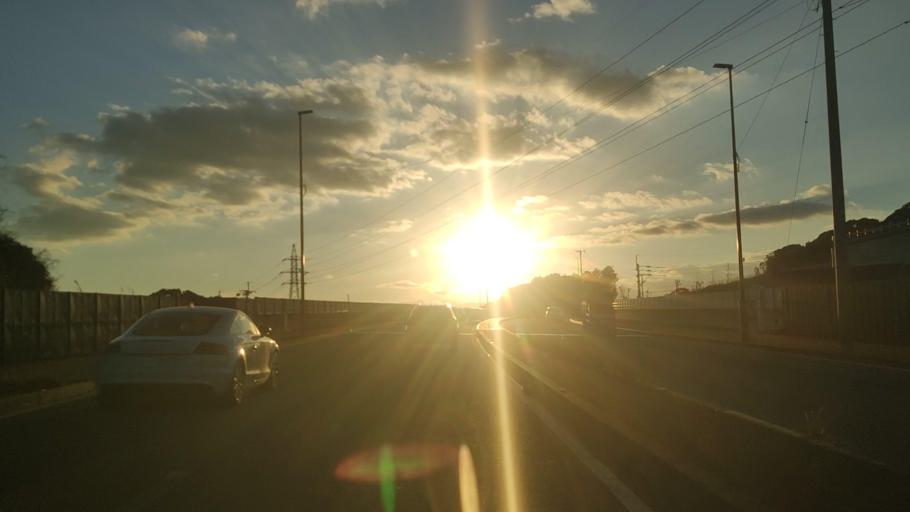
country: JP
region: Fukuoka
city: Onojo
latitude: 33.5538
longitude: 130.4922
